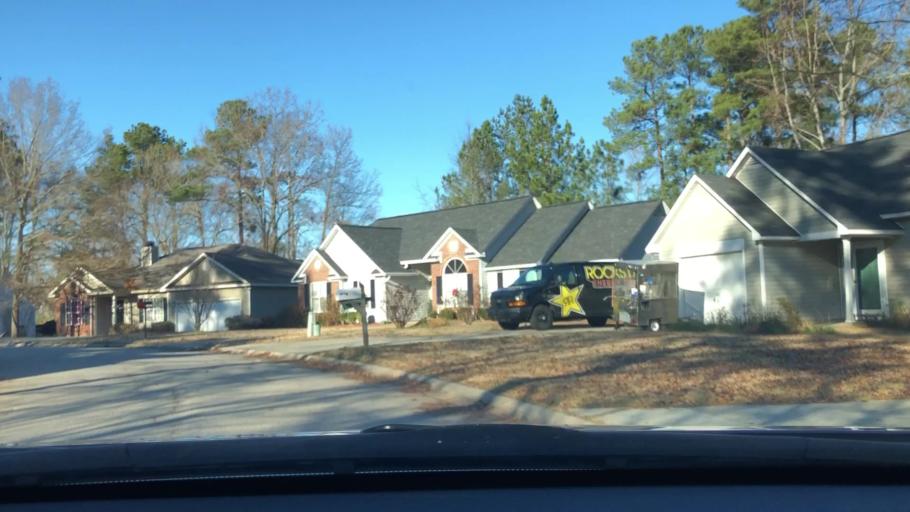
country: US
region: South Carolina
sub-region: Lexington County
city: Irmo
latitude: 34.1175
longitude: -81.1752
